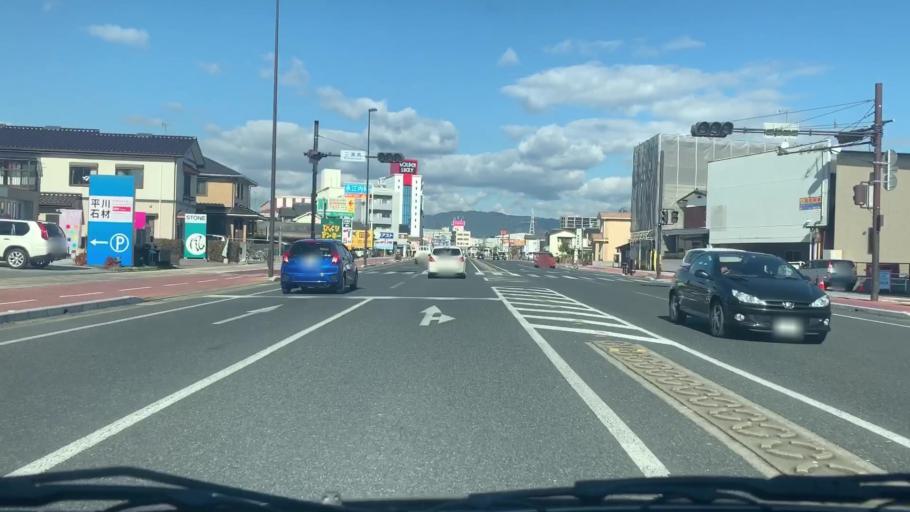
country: JP
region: Saga Prefecture
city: Saga-shi
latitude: 33.2684
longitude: 130.2938
